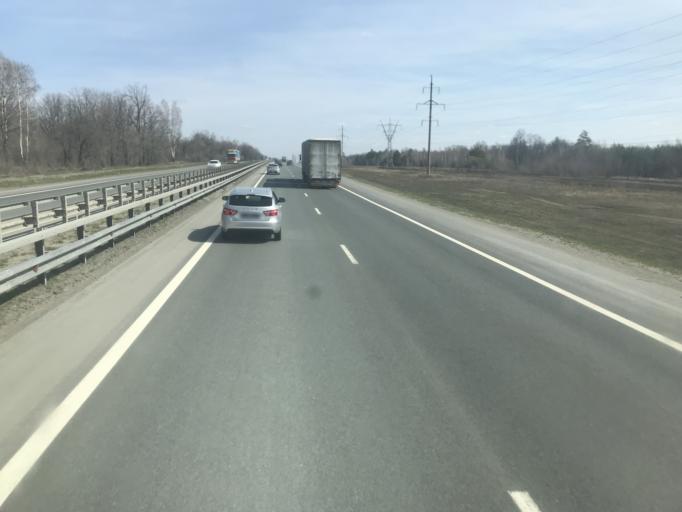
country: RU
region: Samara
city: Pribrezhnyy
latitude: 53.5173
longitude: 49.7930
